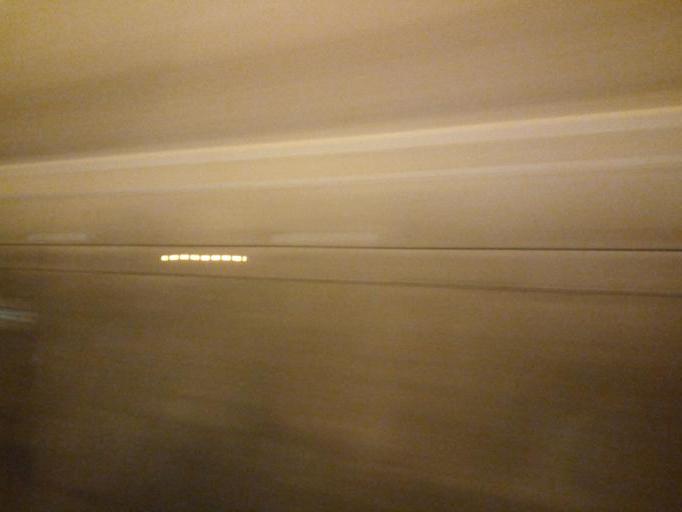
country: DZ
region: Boumerdes
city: Arbatache
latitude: 36.5755
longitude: 3.4110
